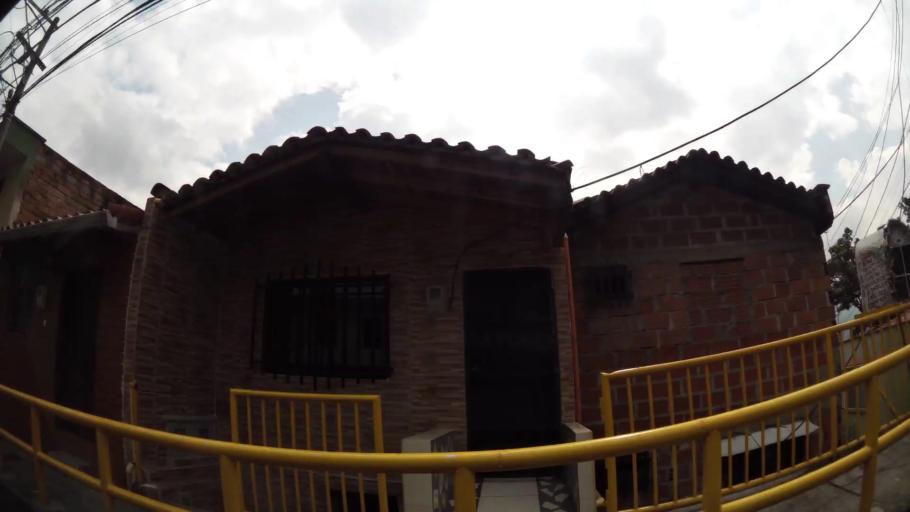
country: CO
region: Antioquia
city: Itagui
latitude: 6.2001
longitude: -75.5905
